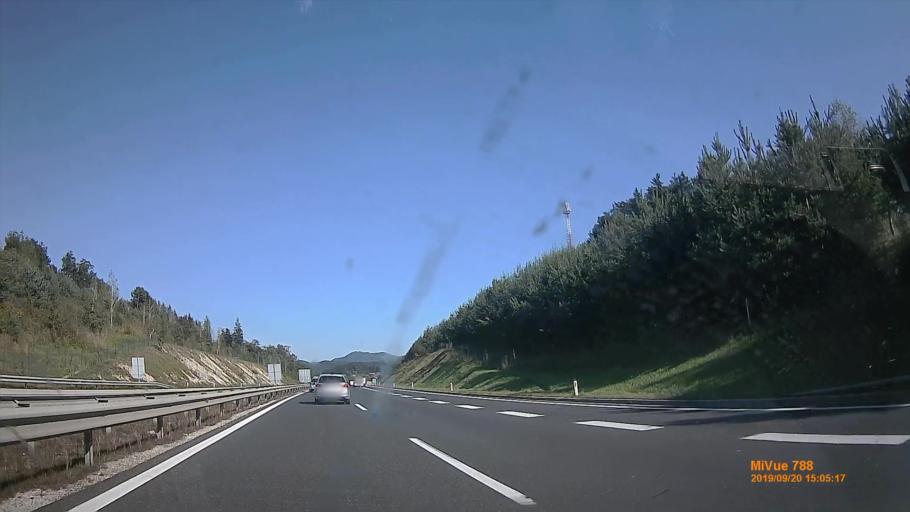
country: SI
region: Domzale
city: Dob
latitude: 46.1549
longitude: 14.6551
